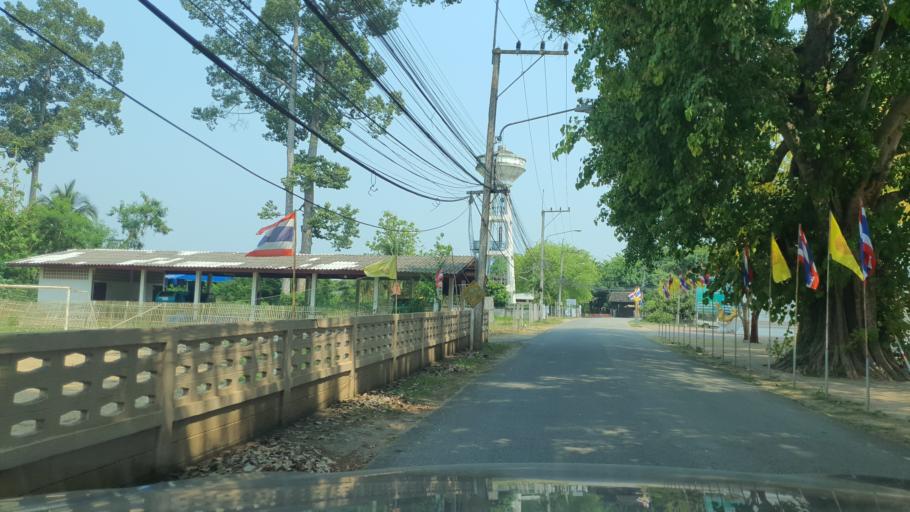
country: TH
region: Chiang Mai
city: Saraphi
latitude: 18.6719
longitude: 98.9855
